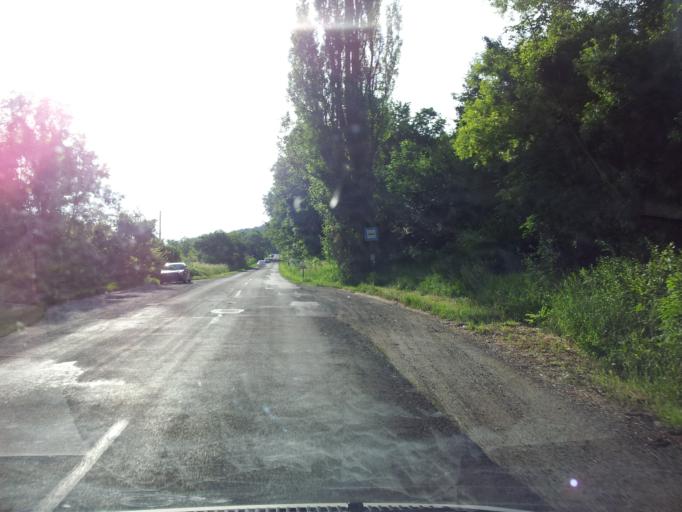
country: HU
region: Komarom-Esztergom
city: Kesztolc
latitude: 47.7451
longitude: 18.8040
